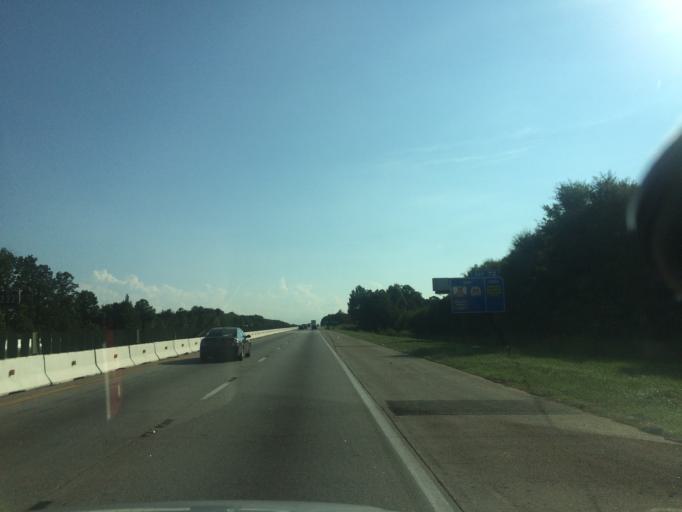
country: US
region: South Carolina
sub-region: Spartanburg County
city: Valley Falls
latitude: 35.0080
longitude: -81.9815
